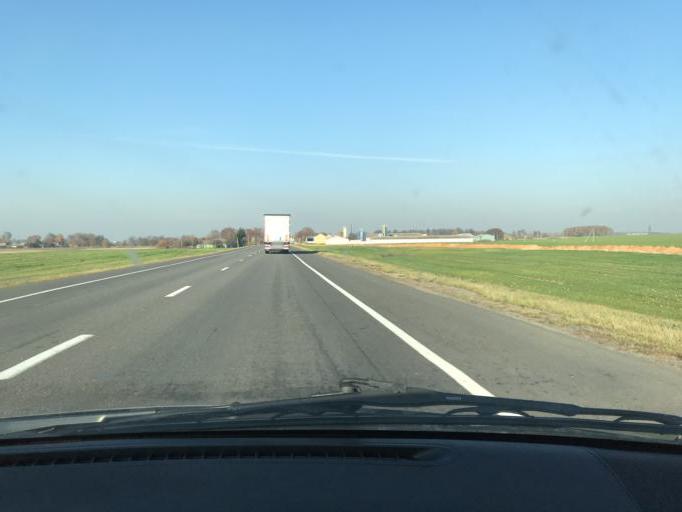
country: BY
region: Mogilev
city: Shklow
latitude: 54.2432
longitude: 30.4511
